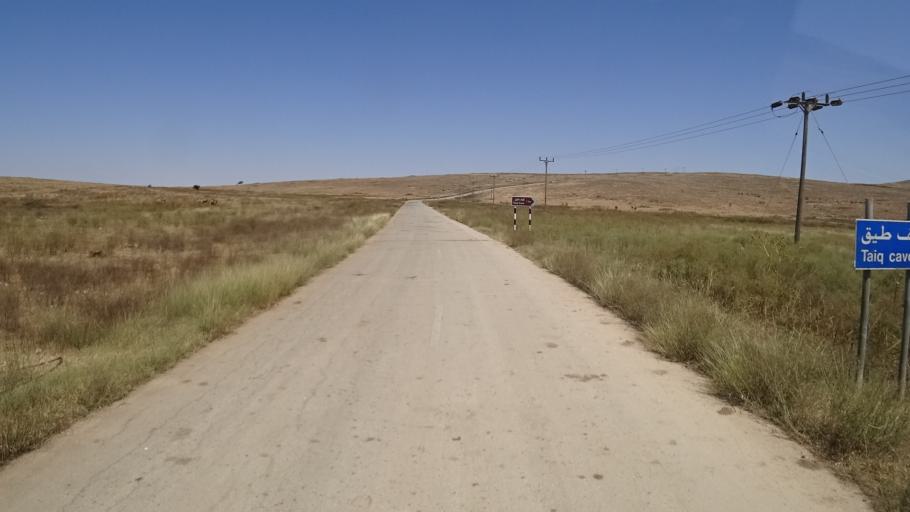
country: OM
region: Zufar
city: Salalah
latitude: 17.1538
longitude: 54.6183
